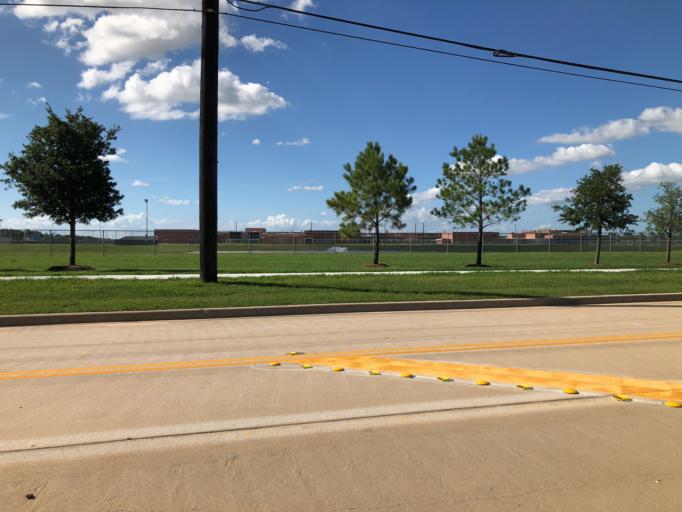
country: US
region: Texas
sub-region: Harris County
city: Katy
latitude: 29.8387
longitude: -95.7773
